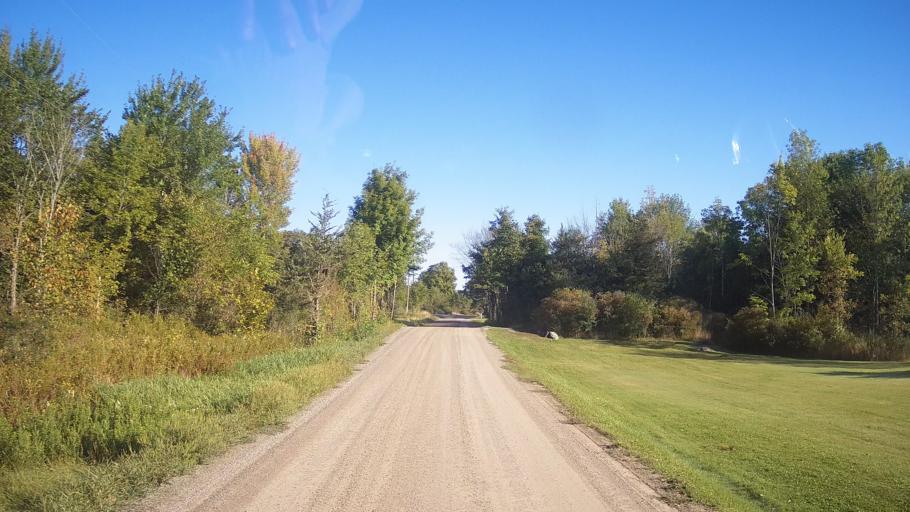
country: US
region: New York
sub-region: Jefferson County
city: Alexandria Bay
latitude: 44.4152
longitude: -75.9771
